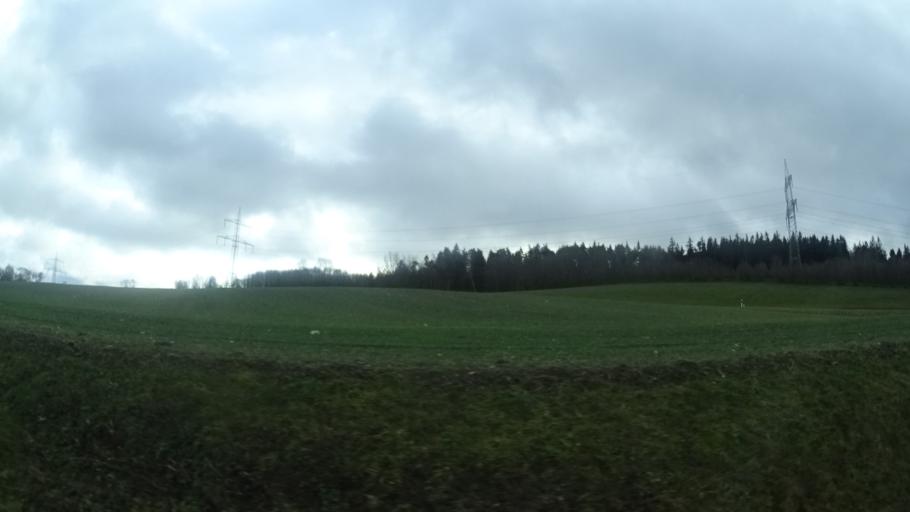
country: DE
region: Thuringia
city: Wittgendorf
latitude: 50.6025
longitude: 11.2697
